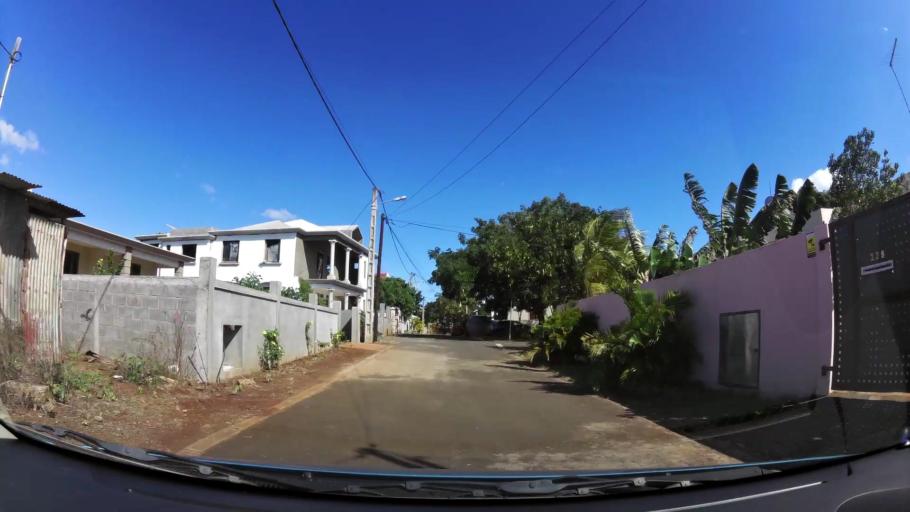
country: MU
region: Black River
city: Albion
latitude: -20.2250
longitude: 57.4152
